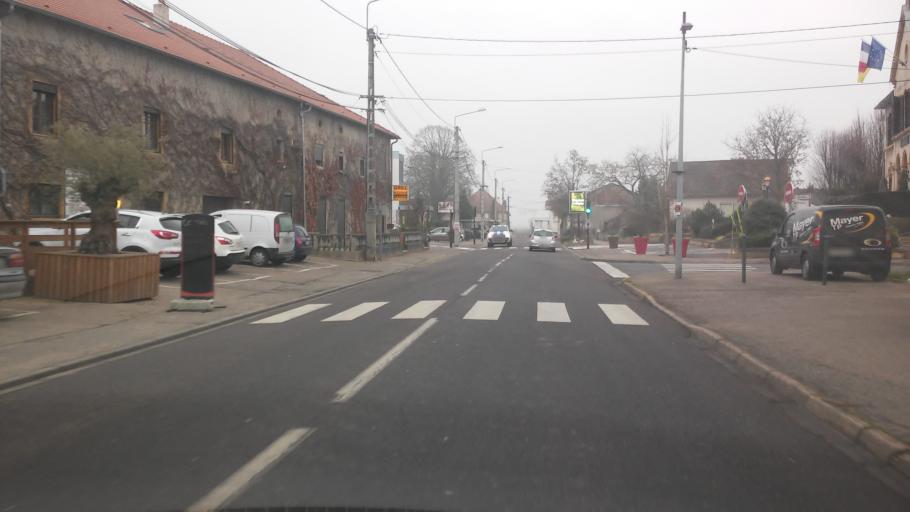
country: FR
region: Lorraine
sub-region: Departement de la Moselle
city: Augny
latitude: 49.0593
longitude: 6.1213
